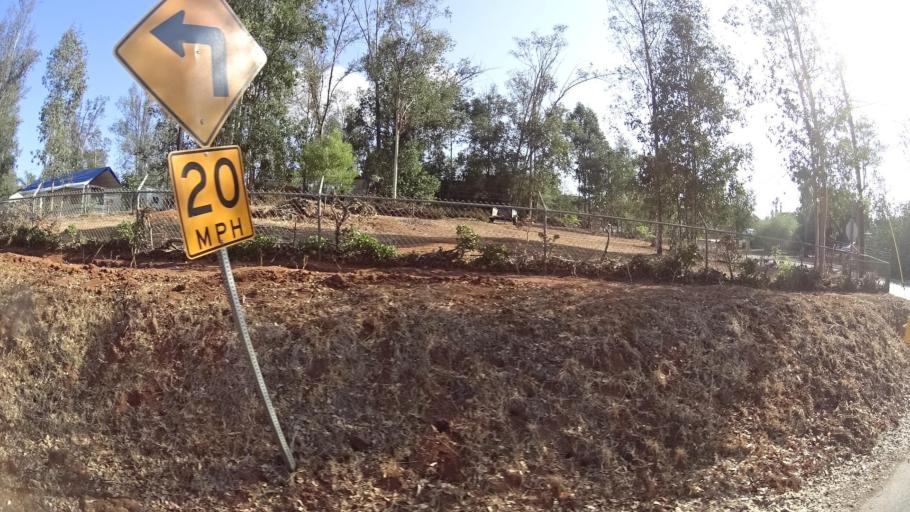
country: US
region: California
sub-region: San Diego County
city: Eucalyptus Hills
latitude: 32.8877
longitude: -116.9461
